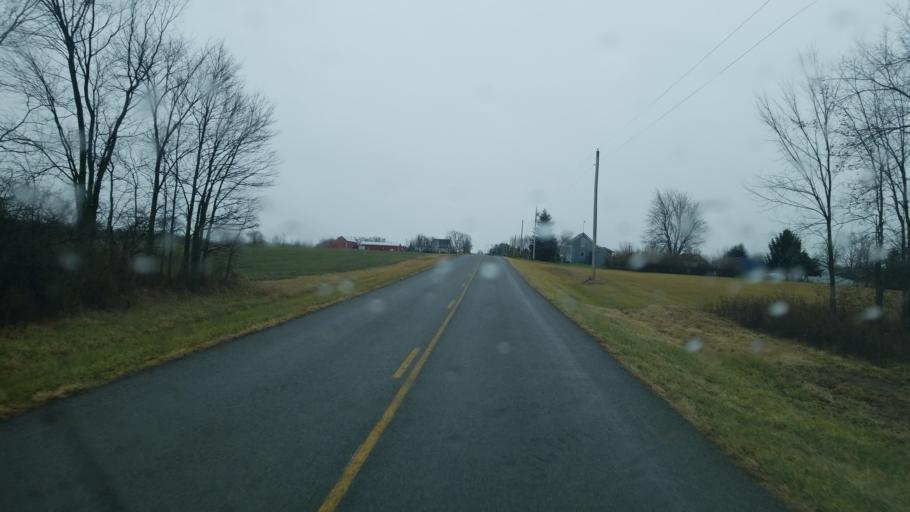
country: US
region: Ohio
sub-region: Logan County
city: Northwood
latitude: 40.4583
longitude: -83.6566
